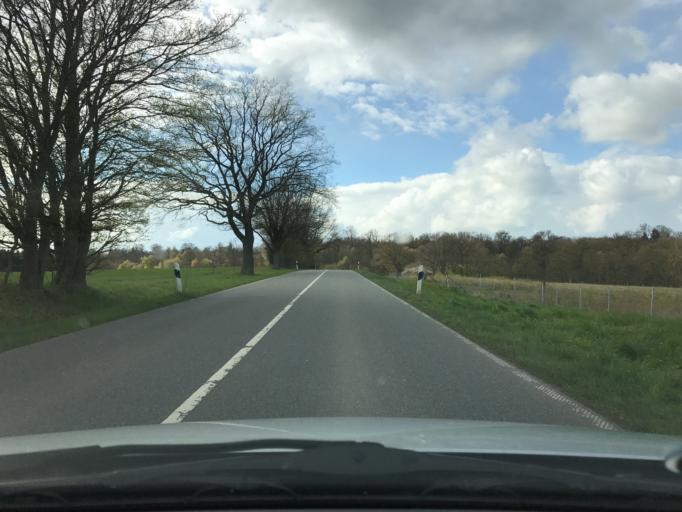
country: DE
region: Schleswig-Holstein
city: Schonwalde am Bungsberg
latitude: 54.1743
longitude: 10.7790
